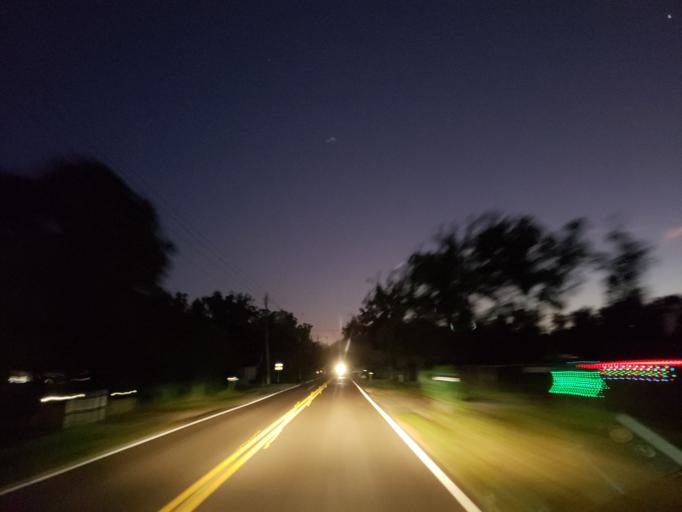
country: US
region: Florida
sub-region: Hillsborough County
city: Dover
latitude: 27.9787
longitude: -82.2198
